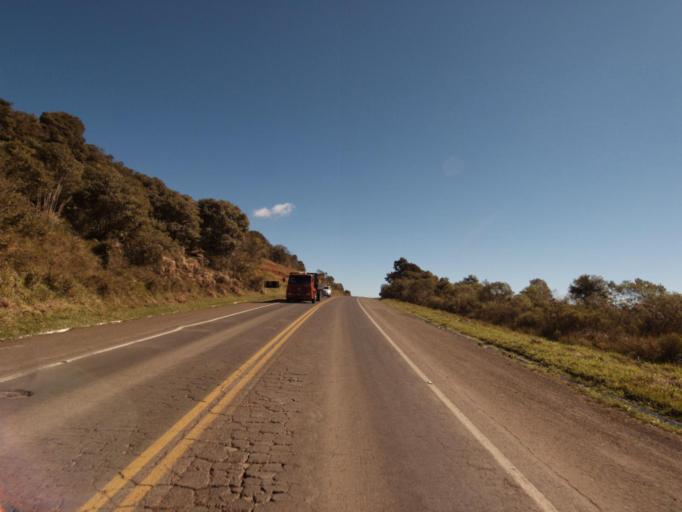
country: BR
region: Santa Catarina
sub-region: Joacaba
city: Joacaba
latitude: -27.1765
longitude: -51.5483
